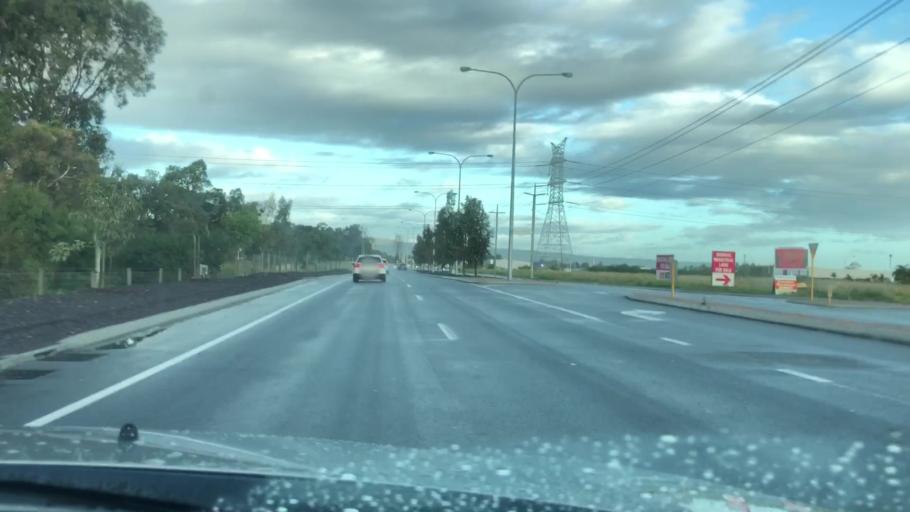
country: AU
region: Western Australia
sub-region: Armadale
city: Seville Grove
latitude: -32.1338
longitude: 115.9663
